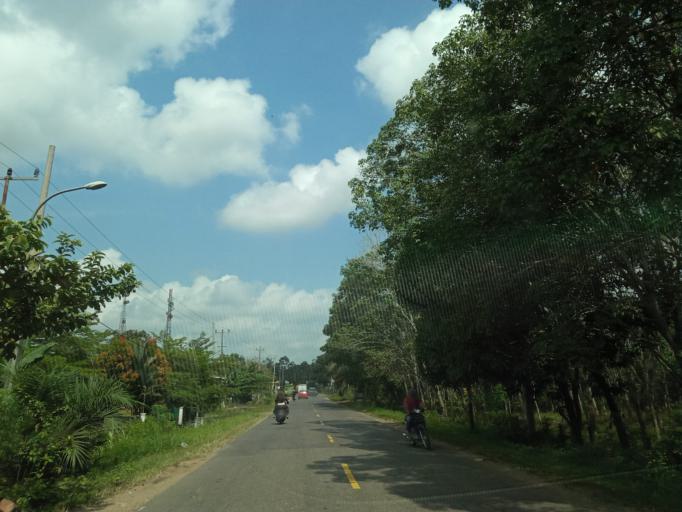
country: ID
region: Jambi
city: Muara Tembesi
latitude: -1.7174
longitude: 103.1250
